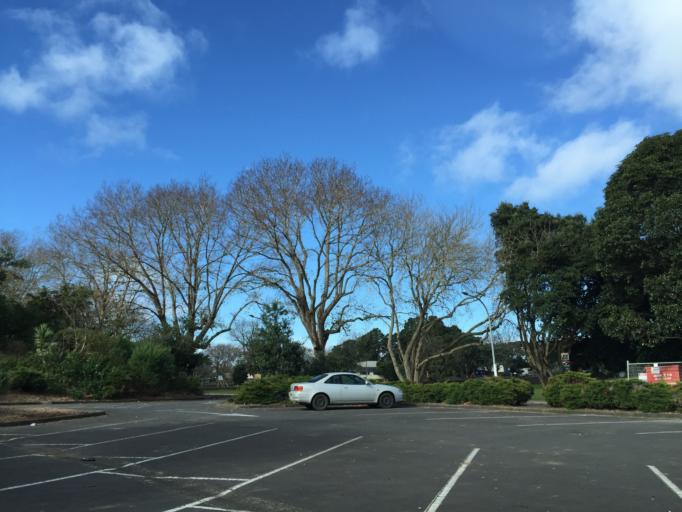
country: NZ
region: Auckland
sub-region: Auckland
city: Auckland
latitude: -36.9076
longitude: 174.7568
